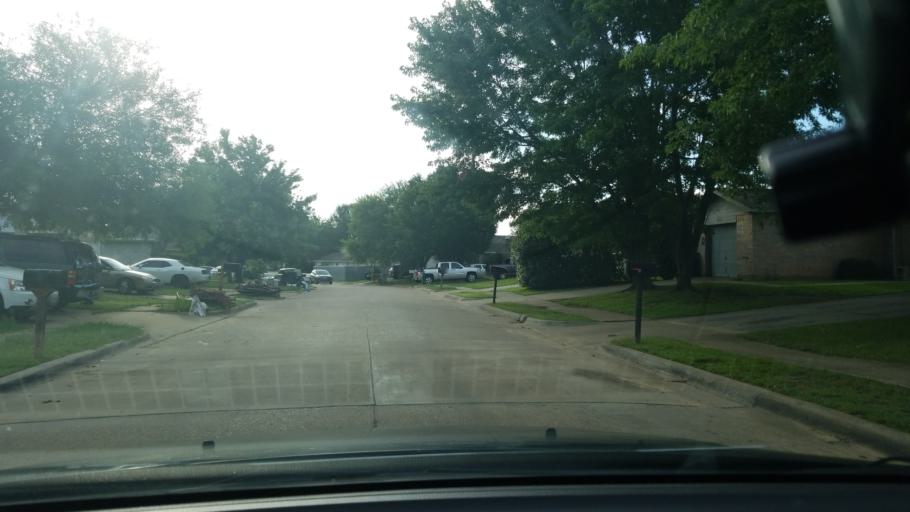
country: US
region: Texas
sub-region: Dallas County
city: Balch Springs
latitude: 32.7534
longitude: -96.6449
